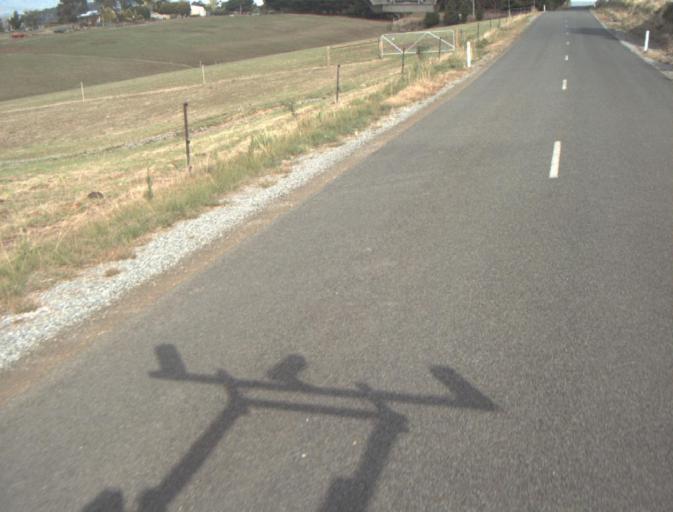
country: AU
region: Tasmania
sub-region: Launceston
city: Mayfield
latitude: -41.2139
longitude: 147.1349
